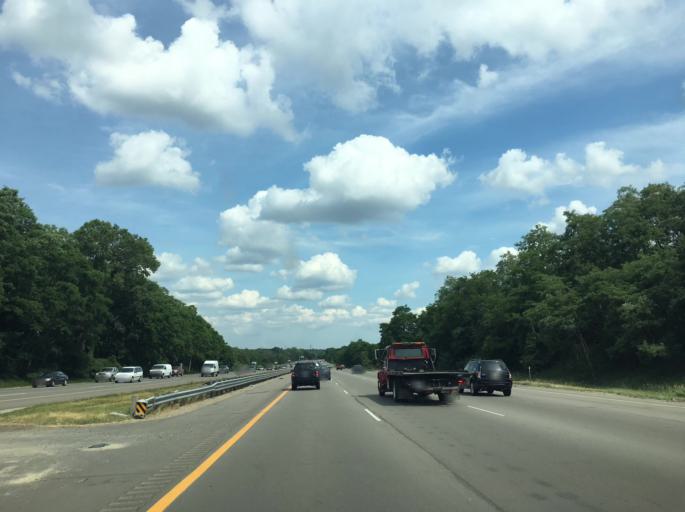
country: US
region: Michigan
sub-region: Oakland County
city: Clarkston
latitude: 42.7308
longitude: -83.3700
